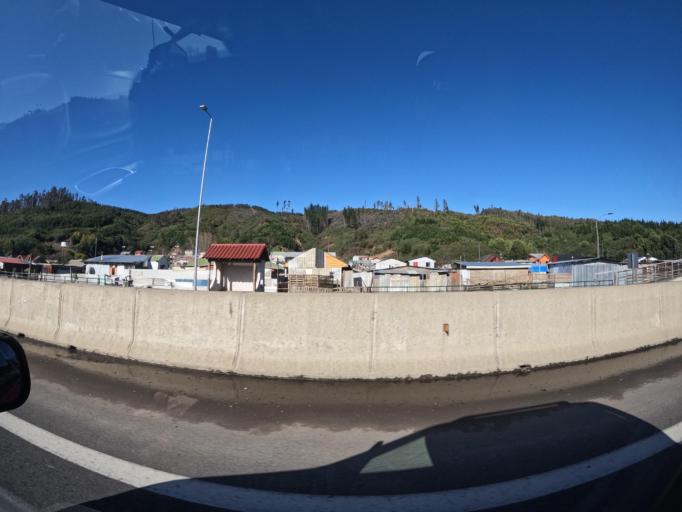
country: CL
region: Biobio
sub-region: Provincia de Concepcion
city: Penco
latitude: -36.8001
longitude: -72.9556
